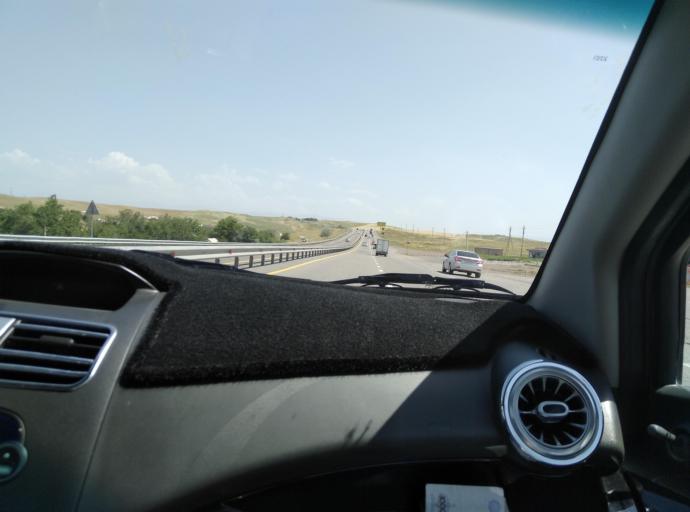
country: UZ
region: Toshkent
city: Ohangaron
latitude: 40.9763
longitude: 69.5441
